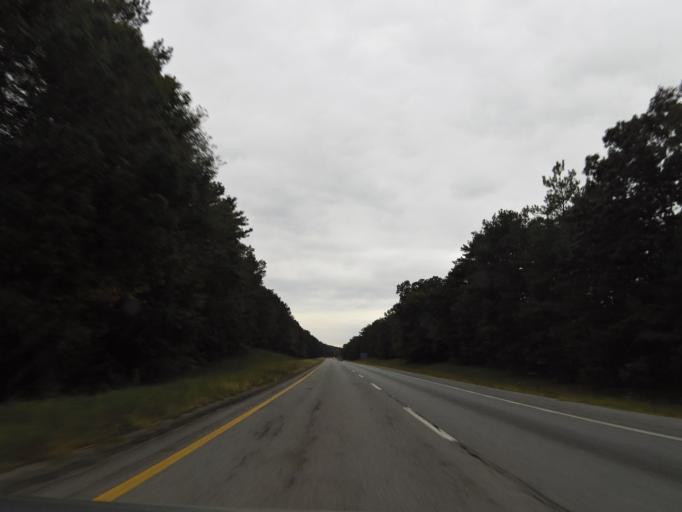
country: US
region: Alabama
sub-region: Saint Clair County
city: Ashville
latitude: 33.8817
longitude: -86.2602
